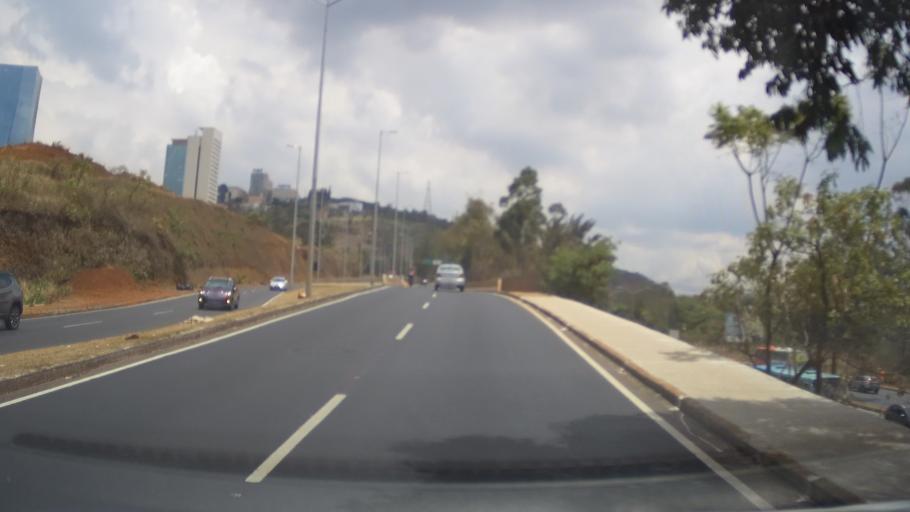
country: BR
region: Minas Gerais
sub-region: Belo Horizonte
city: Belo Horizonte
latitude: -19.9782
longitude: -43.9476
